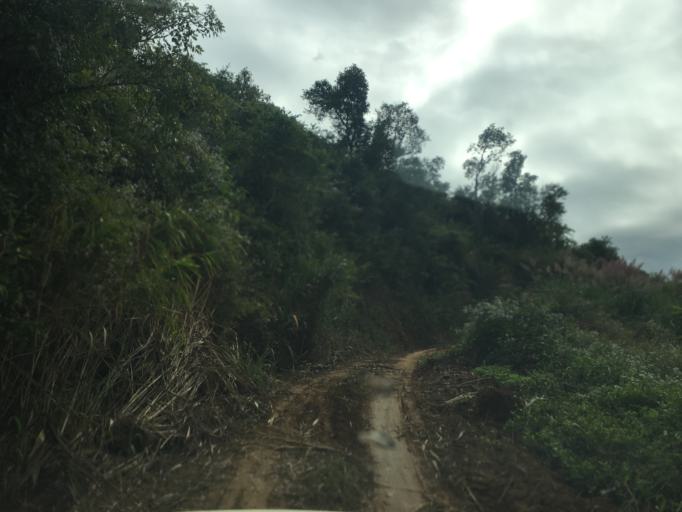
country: LA
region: Houaphan
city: Viengthong
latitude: 19.9263
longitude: 103.2958
